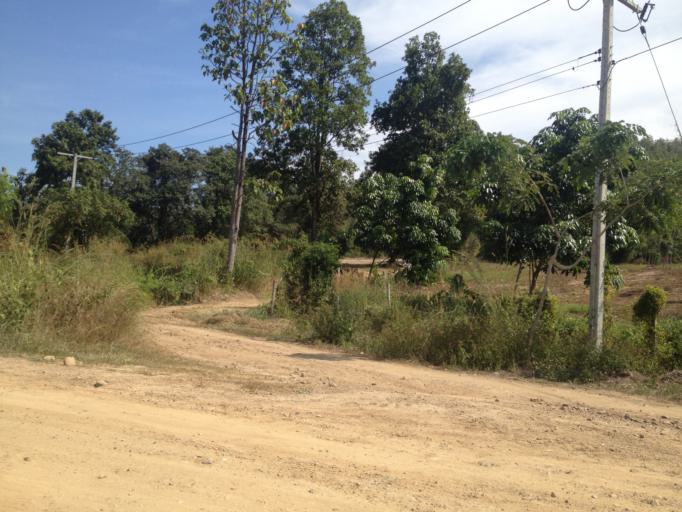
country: TH
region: Chiang Mai
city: Hang Dong
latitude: 18.6982
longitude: 98.8728
